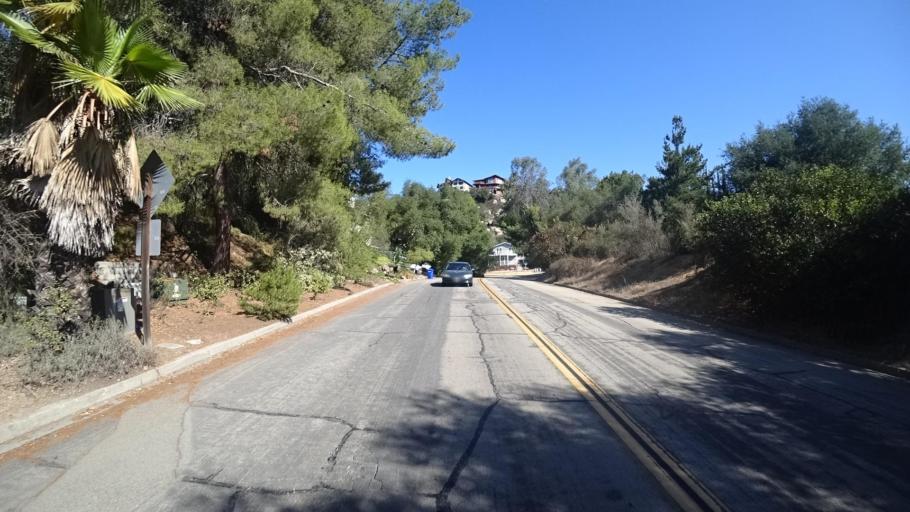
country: US
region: California
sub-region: San Diego County
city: Hidden Meadows
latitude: 33.2163
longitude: -117.1187
